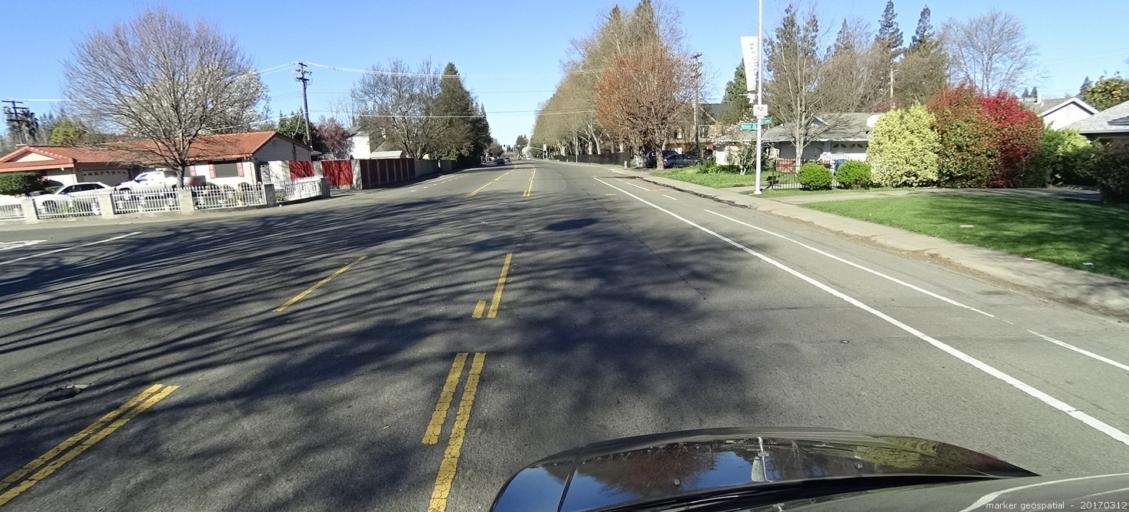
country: US
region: California
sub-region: Sacramento County
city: Sacramento
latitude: 38.6129
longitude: -121.4901
